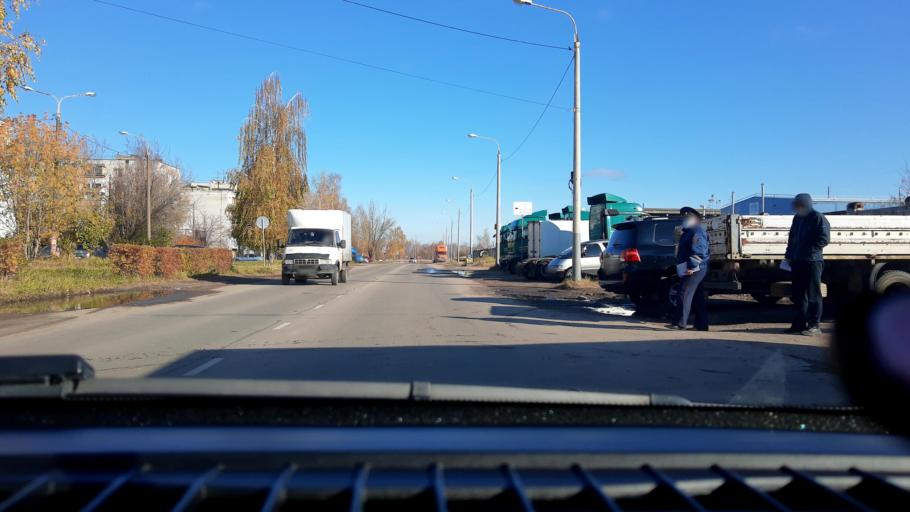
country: RU
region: Nizjnij Novgorod
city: Kstovo
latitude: 56.1486
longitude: 44.2184
